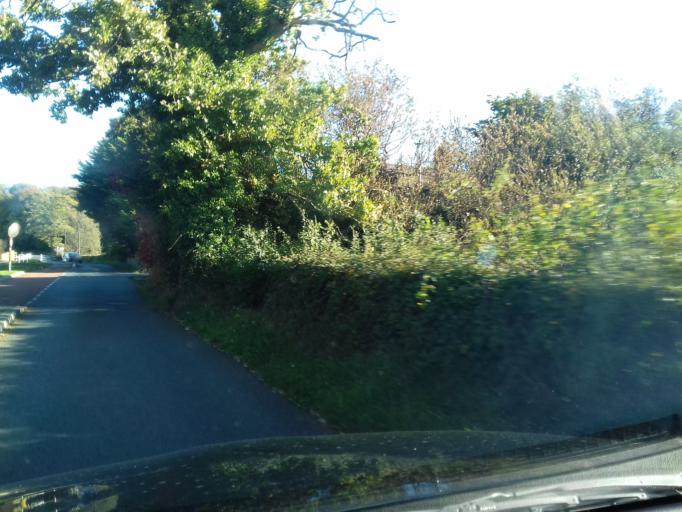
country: IE
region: Leinster
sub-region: Lu
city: Tullyallen
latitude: 53.7197
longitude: -6.4063
